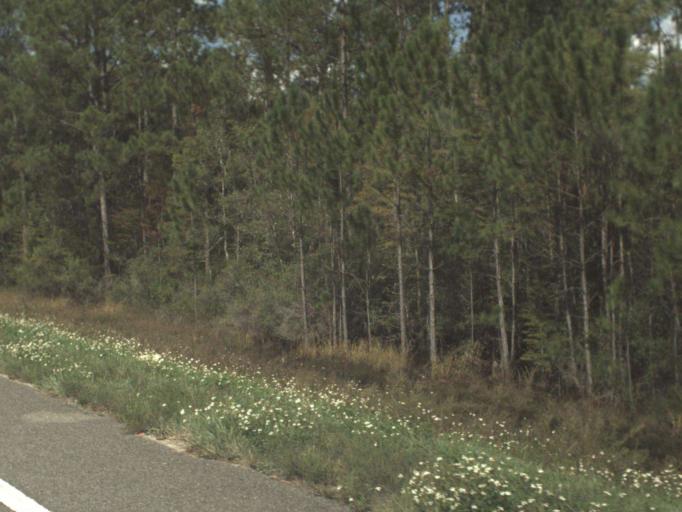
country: US
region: Florida
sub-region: Bay County
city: Laguna Beach
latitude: 30.4573
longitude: -85.9171
